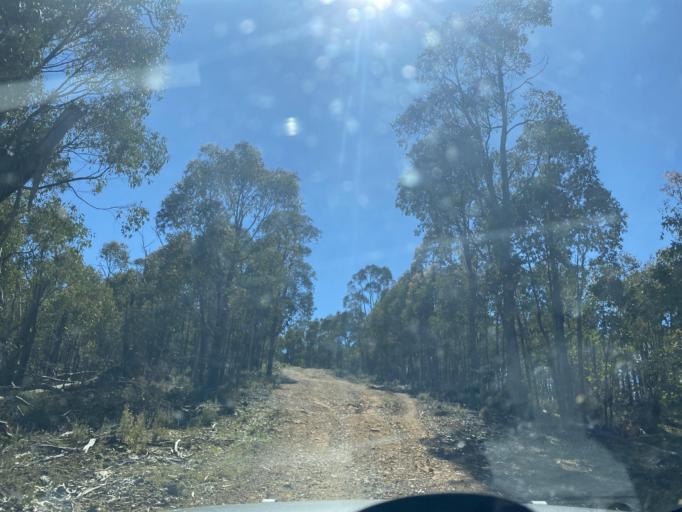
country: AU
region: Victoria
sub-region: Benalla
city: Benalla
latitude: -36.7278
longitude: 146.1822
